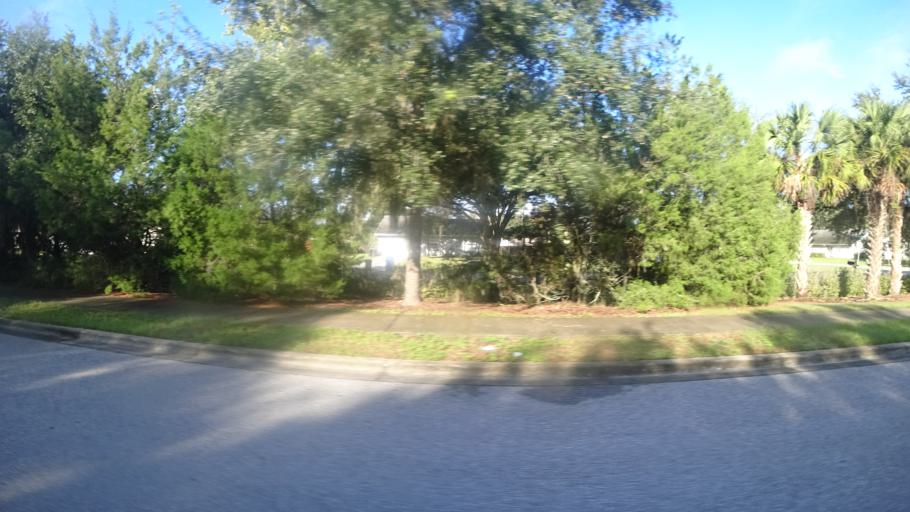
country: US
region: Florida
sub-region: Manatee County
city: Ellenton
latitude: 27.5528
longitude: -82.4620
